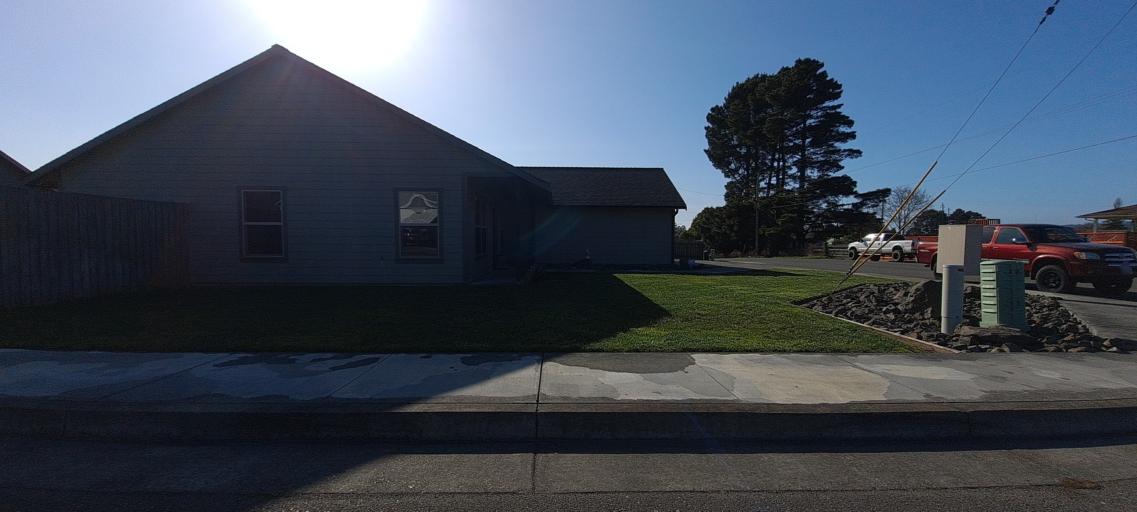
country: US
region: California
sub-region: Humboldt County
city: Fortuna
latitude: 40.5738
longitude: -124.1343
